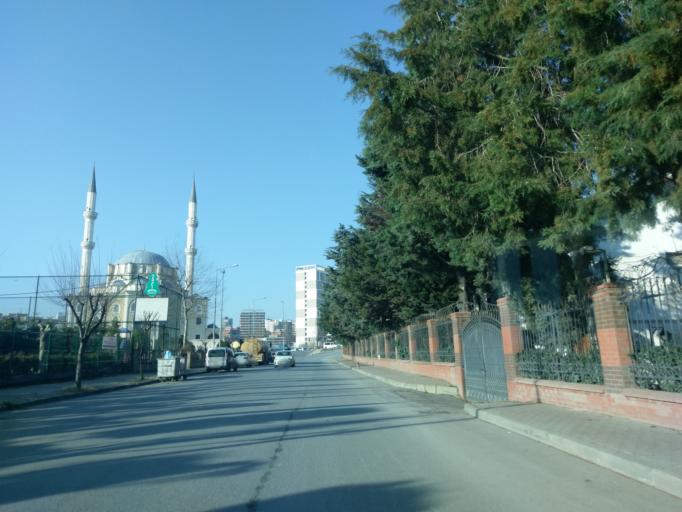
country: TR
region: Istanbul
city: Mahmutbey
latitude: 41.0336
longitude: 28.7659
